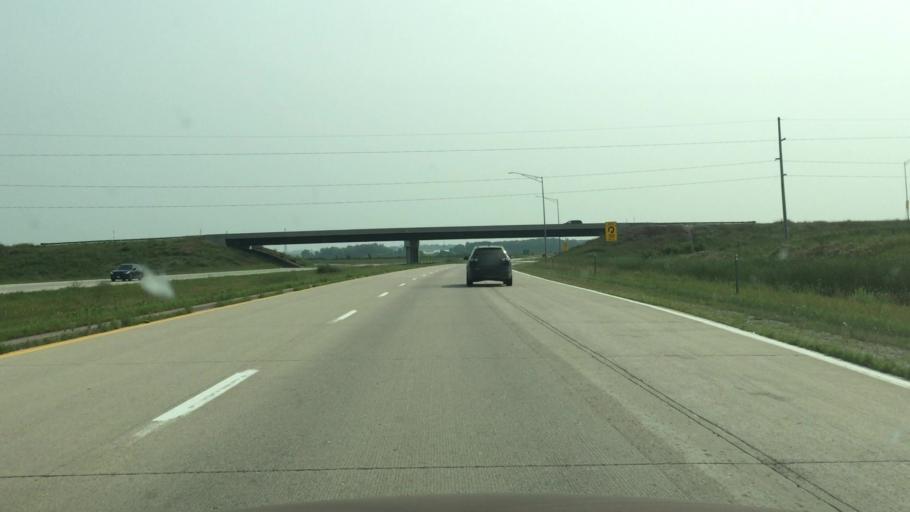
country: US
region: Iowa
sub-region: Osceola County
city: Sibley
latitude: 43.3811
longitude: -95.7529
